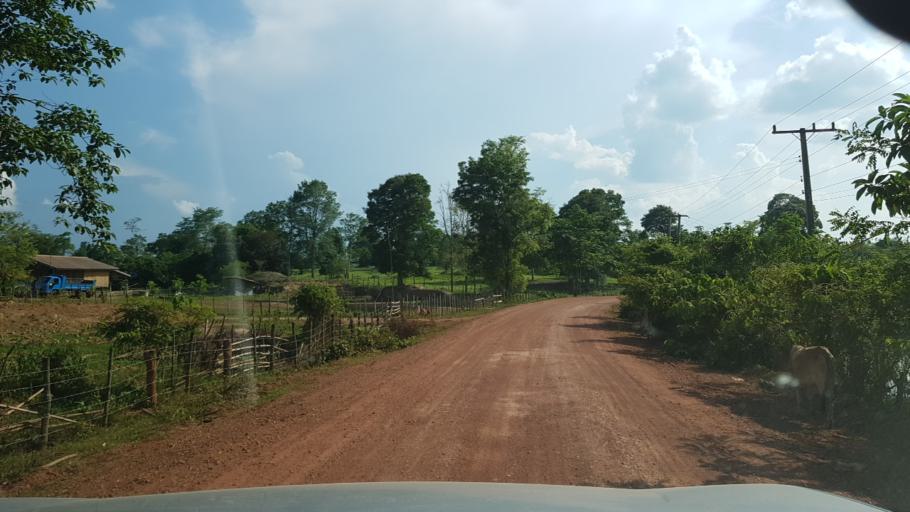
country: LA
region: Vientiane
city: Muang Phon-Hong
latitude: 18.3462
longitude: 102.3043
